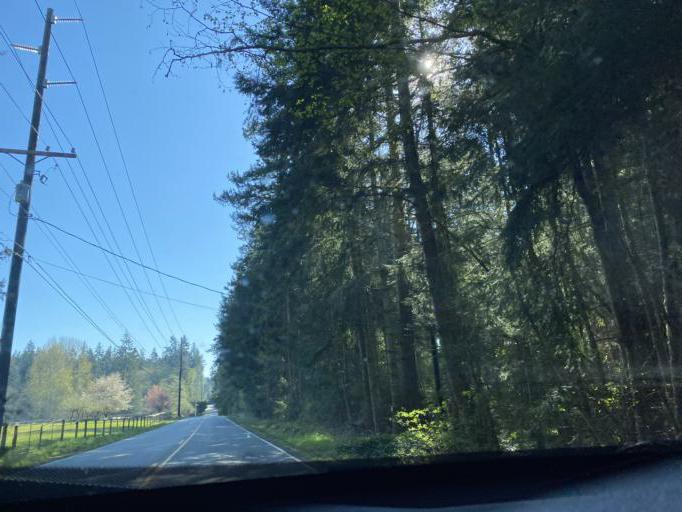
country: US
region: Washington
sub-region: Island County
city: Freeland
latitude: 48.0799
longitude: -122.5918
